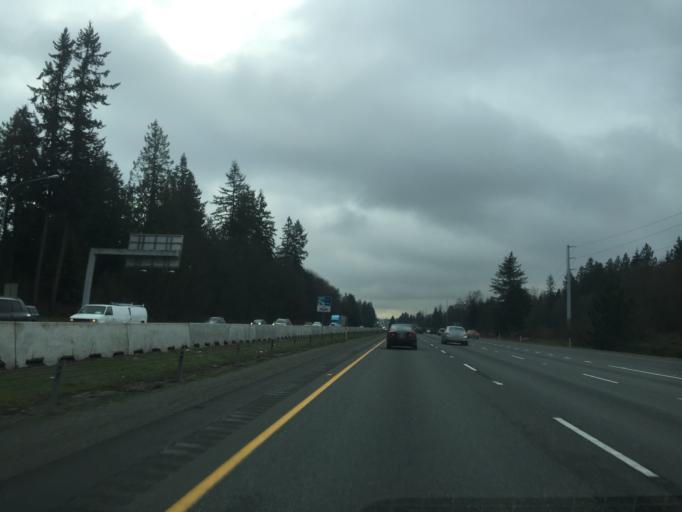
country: US
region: Washington
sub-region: Snohomish County
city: Marysville
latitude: 48.0720
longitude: -122.1849
